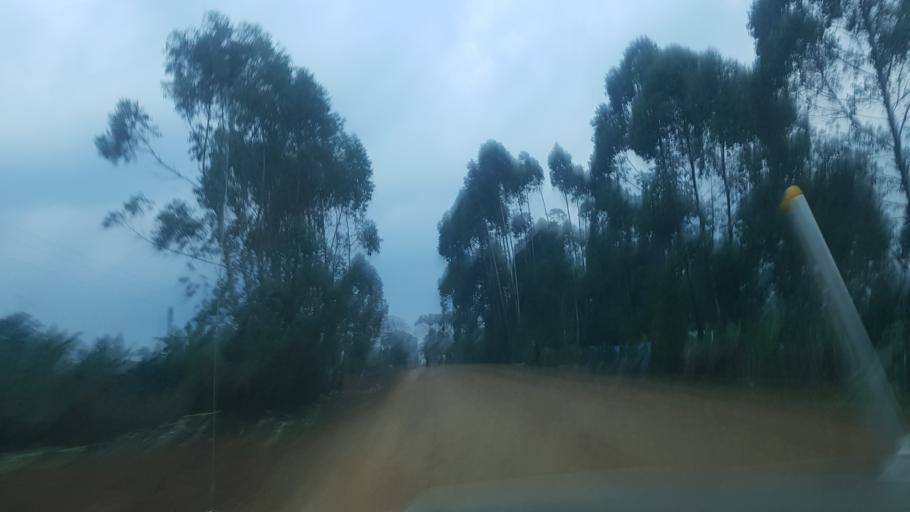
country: ET
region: Oromiya
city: Gore
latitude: 7.7697
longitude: 35.4686
